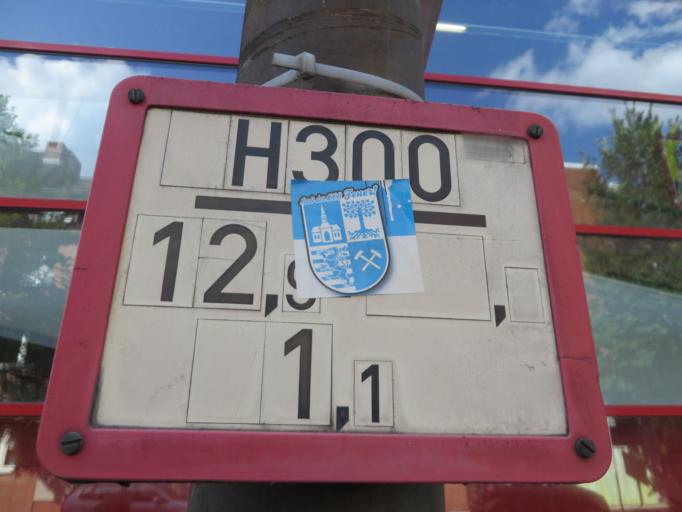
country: DE
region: North Rhine-Westphalia
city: Witten
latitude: 51.4382
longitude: 7.3295
